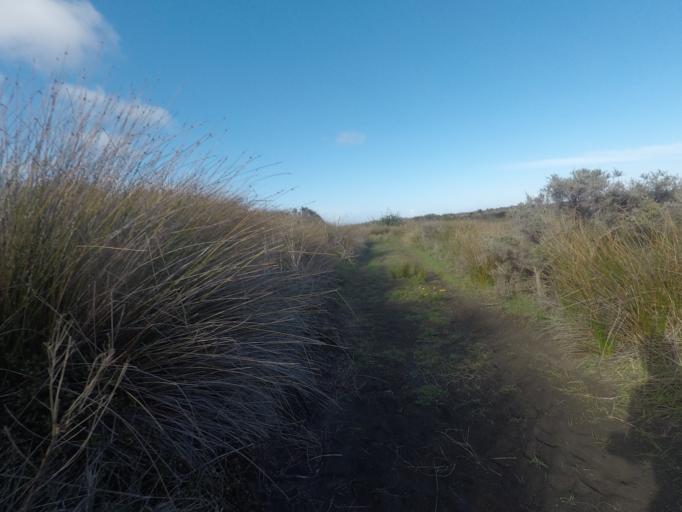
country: NZ
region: Auckland
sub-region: Auckland
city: Titirangi
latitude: -37.0074
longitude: 174.4803
